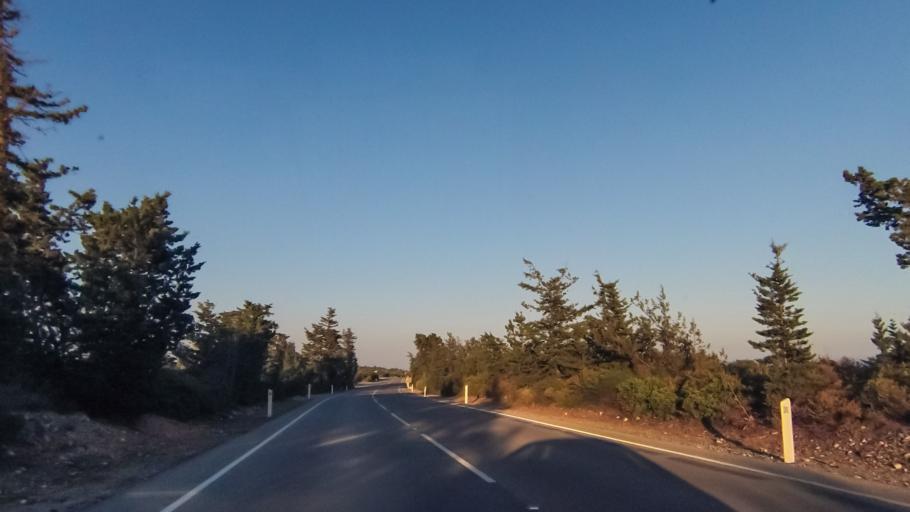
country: CY
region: Limassol
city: Sotira
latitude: 34.6704
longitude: 32.8729
